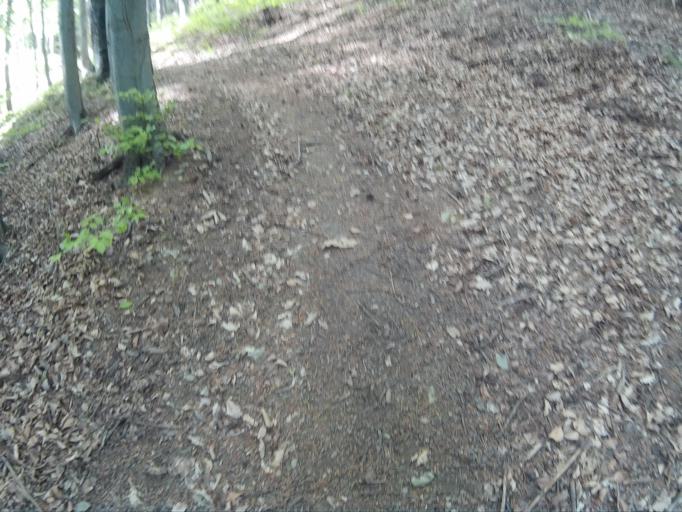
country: AT
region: Burgenland
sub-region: Politischer Bezirk Oberwart
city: Rechnitz
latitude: 47.3554
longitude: 16.4718
